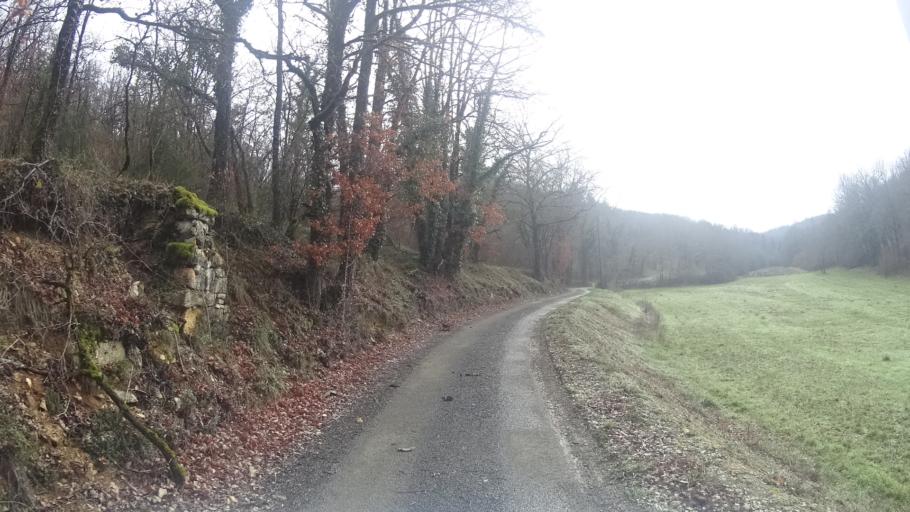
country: FR
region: Aquitaine
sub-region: Departement de la Dordogne
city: Terrasson-Lavilledieu
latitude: 45.1095
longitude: 1.2284
